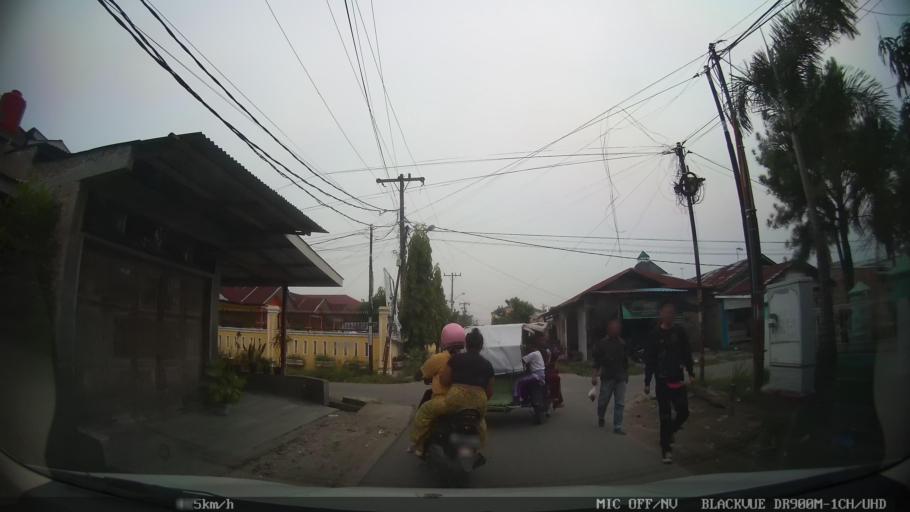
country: ID
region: North Sumatra
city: Medan
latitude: 3.5749
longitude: 98.7323
